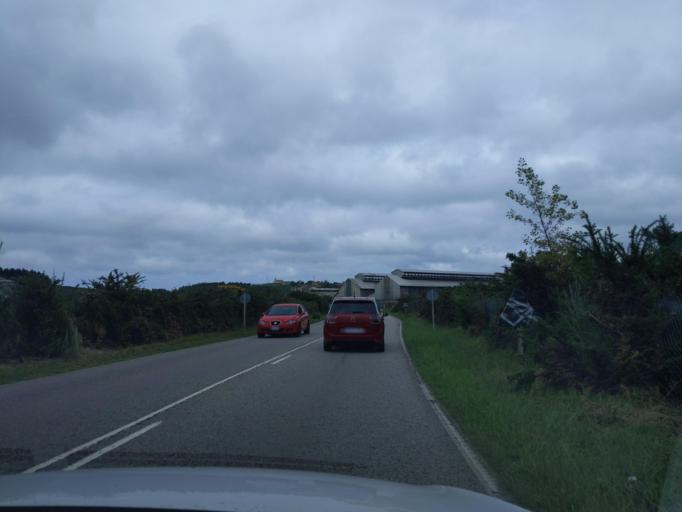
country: ES
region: Asturias
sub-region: Province of Asturias
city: Aviles
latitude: 43.5801
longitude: -5.9177
